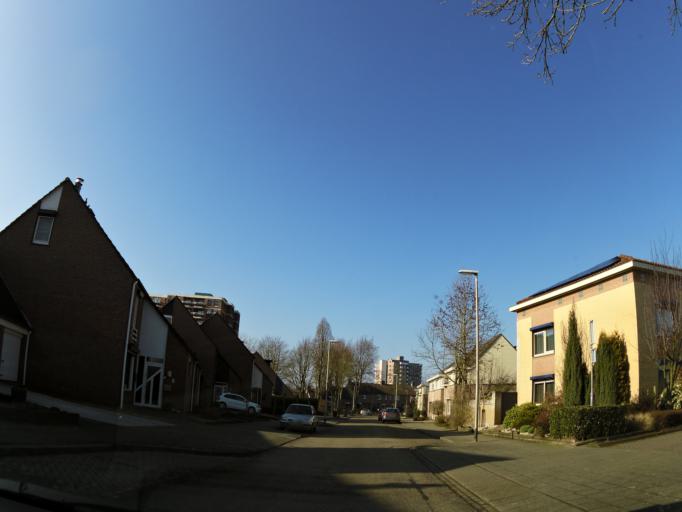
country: NL
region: Limburg
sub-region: Gemeente Heerlen
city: Heerlen
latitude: 50.8722
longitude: 6.0140
